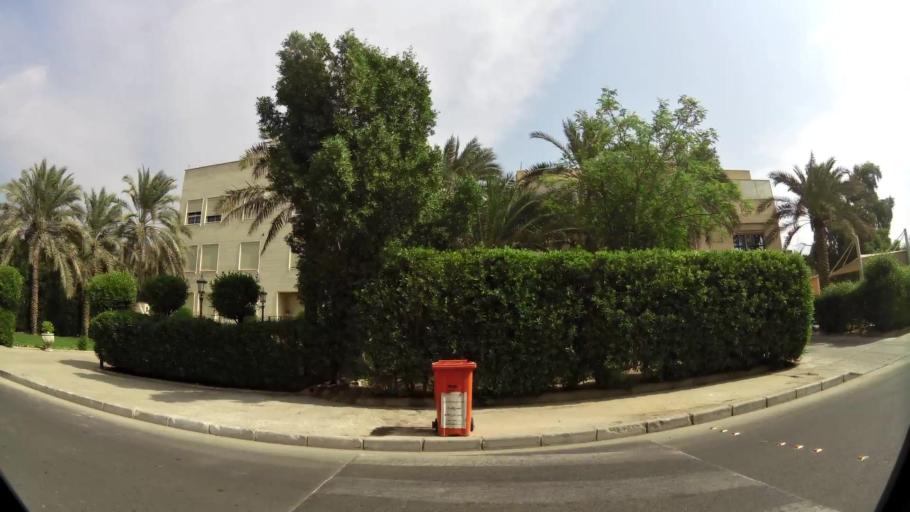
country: KW
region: Al Asimah
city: Ash Shamiyah
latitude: 29.3500
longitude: 47.9753
